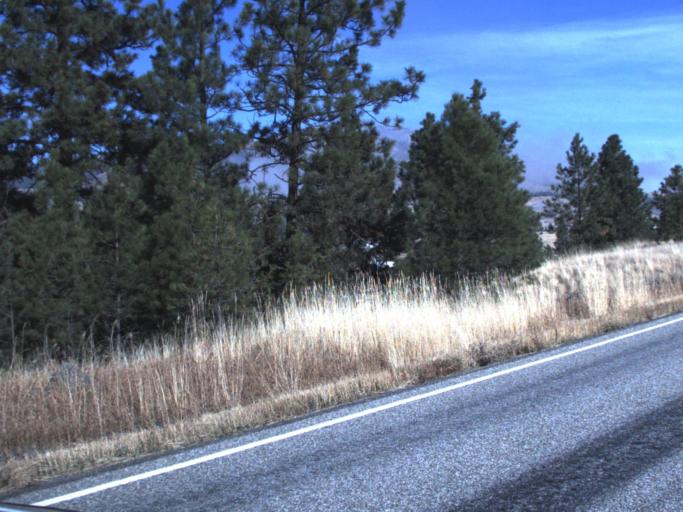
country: US
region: Washington
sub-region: Ferry County
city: Republic
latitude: 48.7476
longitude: -118.6557
